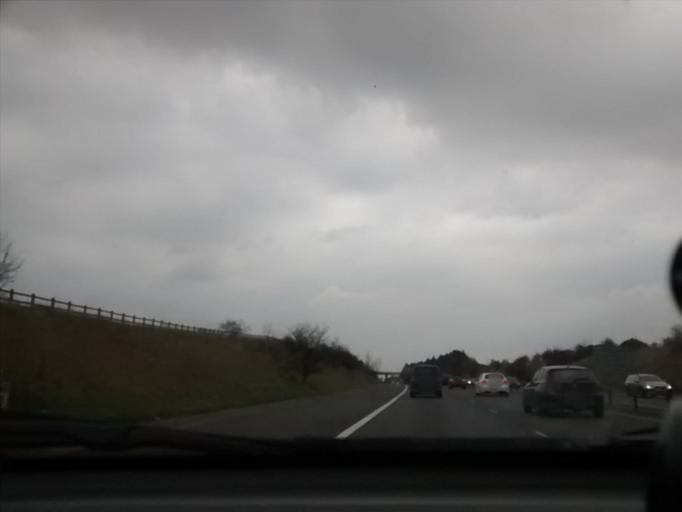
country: GB
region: England
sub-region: Essex
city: Saffron Walden
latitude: 52.0403
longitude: 0.1899
